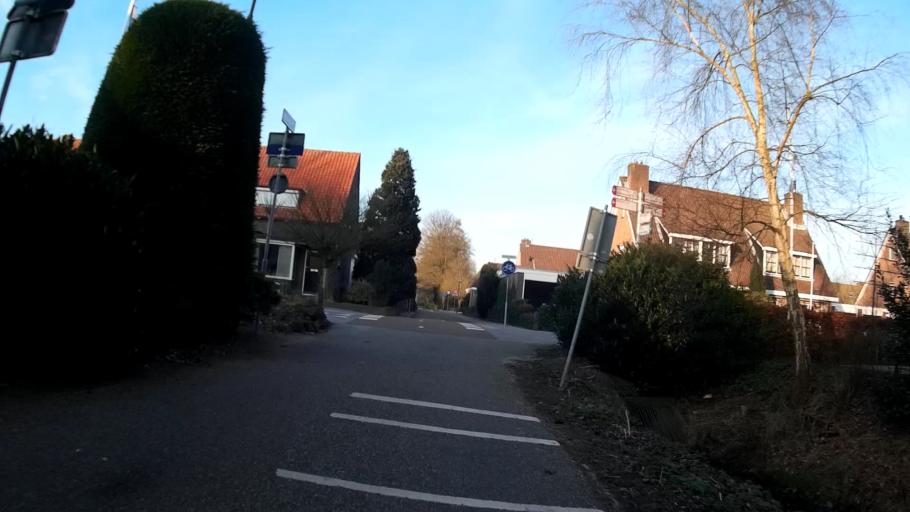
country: NL
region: Utrecht
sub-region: Gemeente Veenendaal
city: Veenendaal
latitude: 52.0221
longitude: 5.5264
